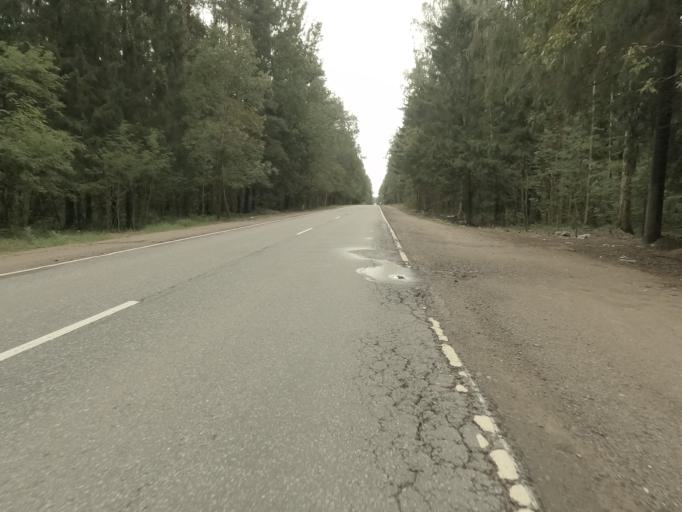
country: RU
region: Leningrad
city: Koltushi
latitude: 59.8954
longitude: 30.7509
